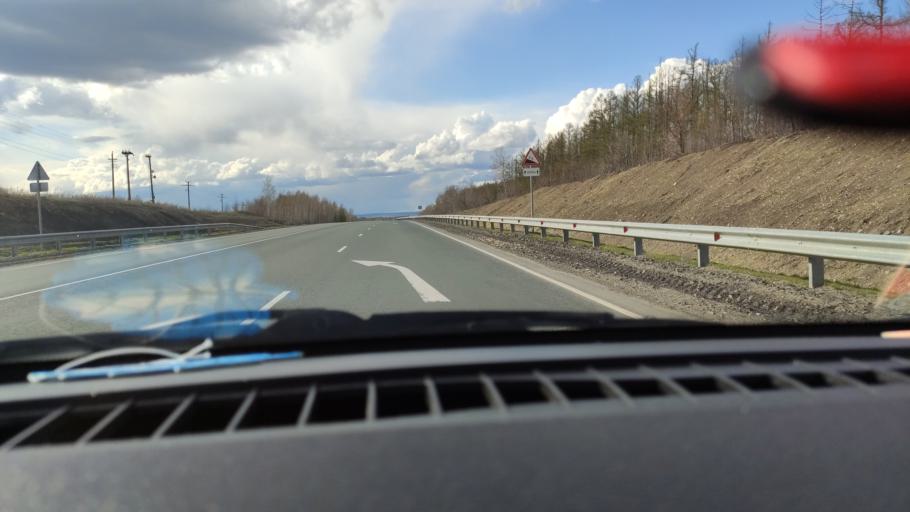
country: RU
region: Saratov
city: Shikhany
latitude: 52.1476
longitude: 47.1941
